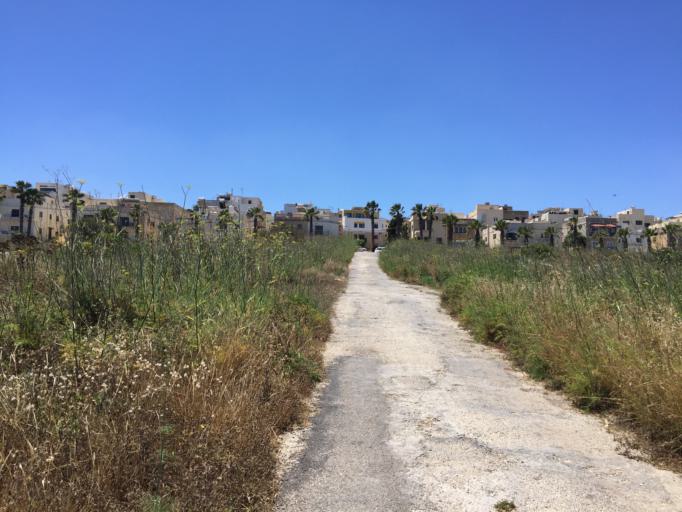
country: MT
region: Pembroke
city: Pembroke
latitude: 35.9297
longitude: 14.4839
